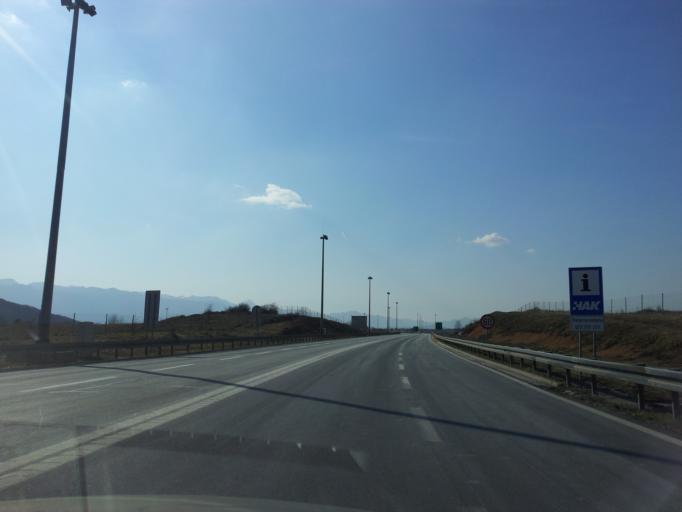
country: HR
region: Zadarska
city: Starigrad
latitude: 44.4396
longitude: 15.6284
